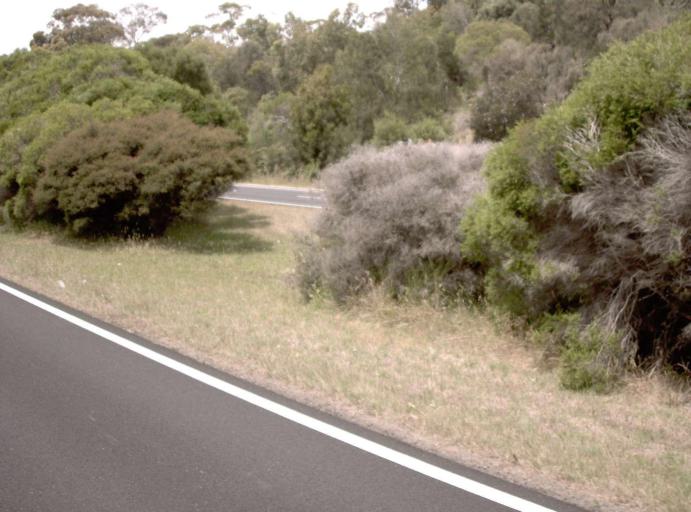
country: AU
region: Victoria
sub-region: Mornington Peninsula
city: McCrae
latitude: -38.3471
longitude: 144.9409
